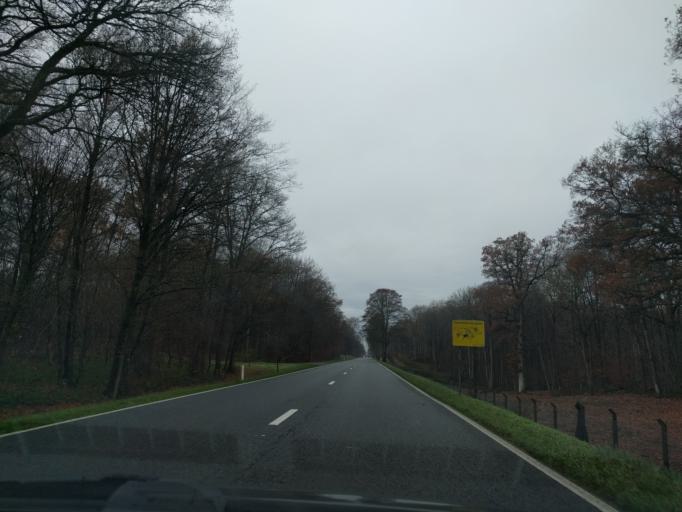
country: BE
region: Wallonia
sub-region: Province de Namur
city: Florennes
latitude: 50.2227
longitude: 4.6460
